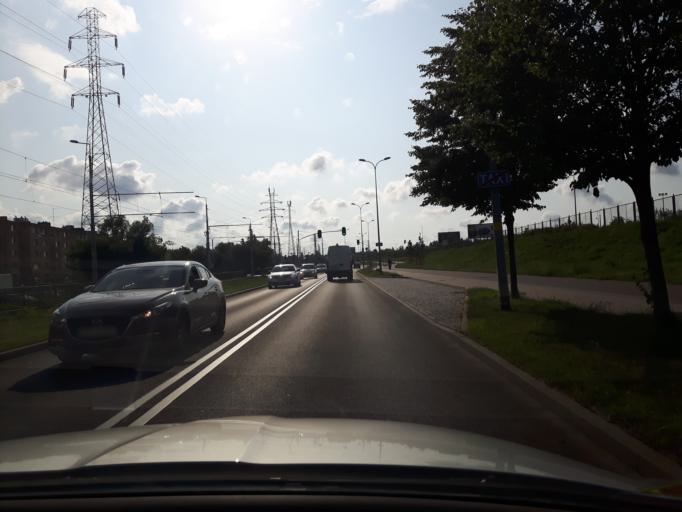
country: PL
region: Pomeranian Voivodeship
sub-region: Gdansk
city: Gdansk
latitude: 54.3385
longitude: 18.6078
